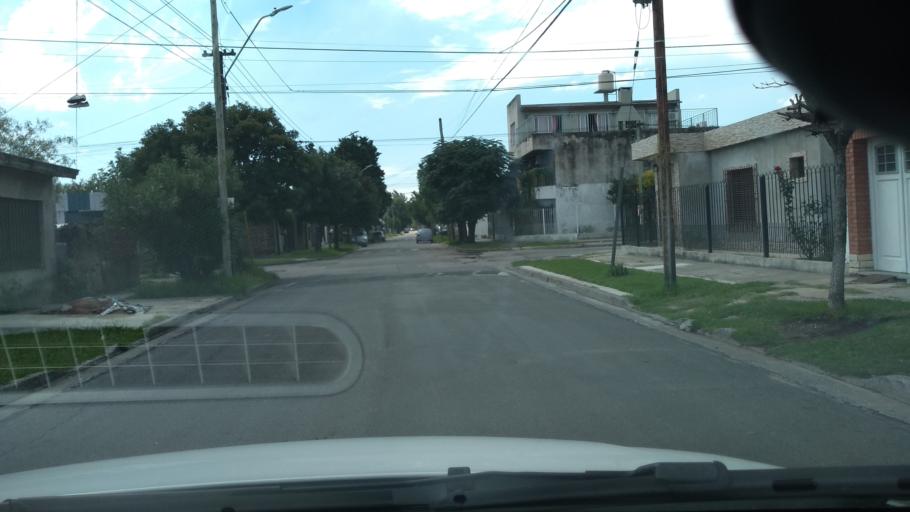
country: AR
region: Buenos Aires
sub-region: Partido de Moron
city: Moron
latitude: -34.6672
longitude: -58.6072
